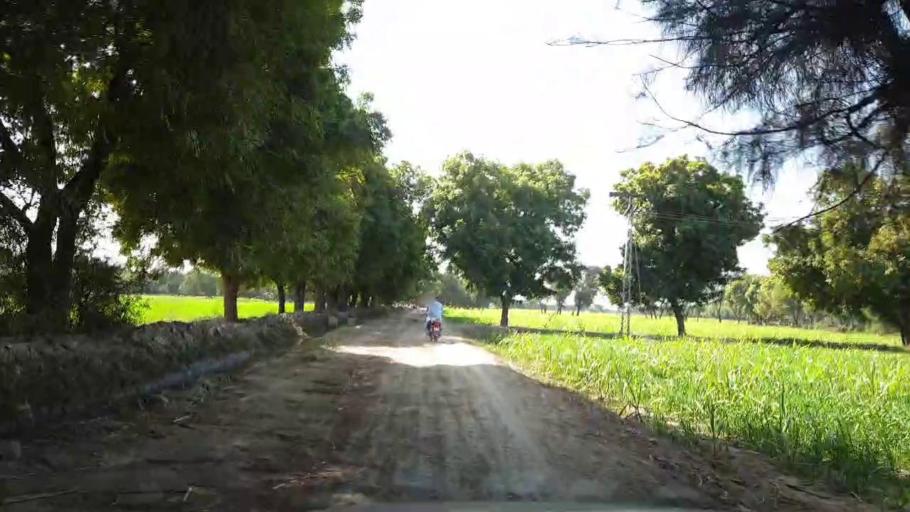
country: PK
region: Sindh
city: Matiari
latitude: 25.5300
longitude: 68.4866
